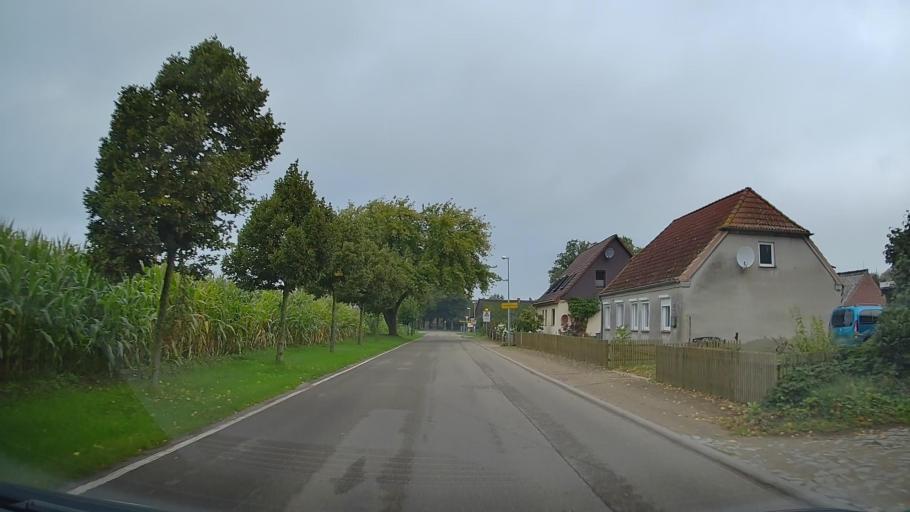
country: DE
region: Mecklenburg-Vorpommern
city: Blowatz
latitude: 53.9626
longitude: 11.5479
